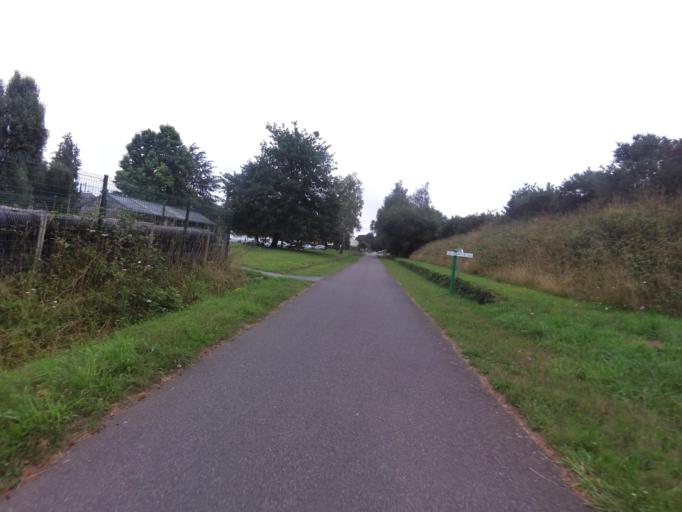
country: FR
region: Brittany
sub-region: Departement du Morbihan
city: Guillac
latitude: 47.8635
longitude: -2.4388
